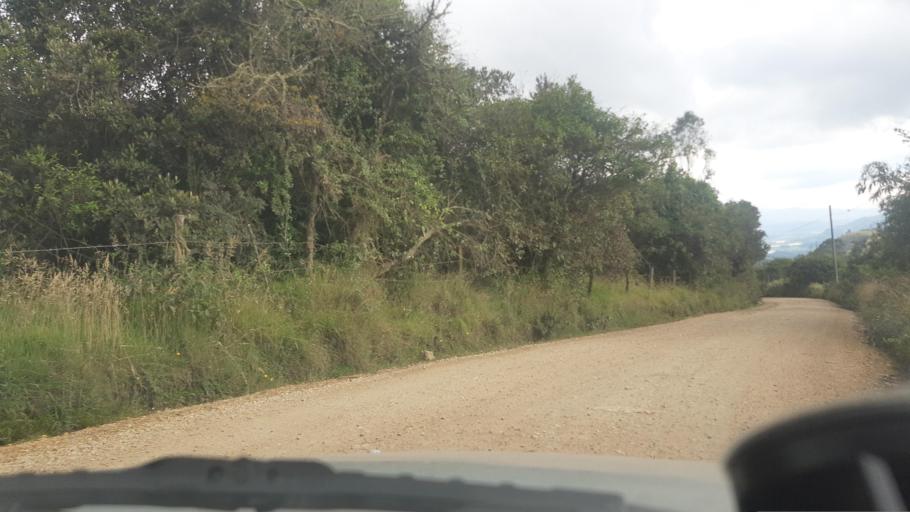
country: CO
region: Cundinamarca
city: Suesca
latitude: 5.1371
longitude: -73.7818
